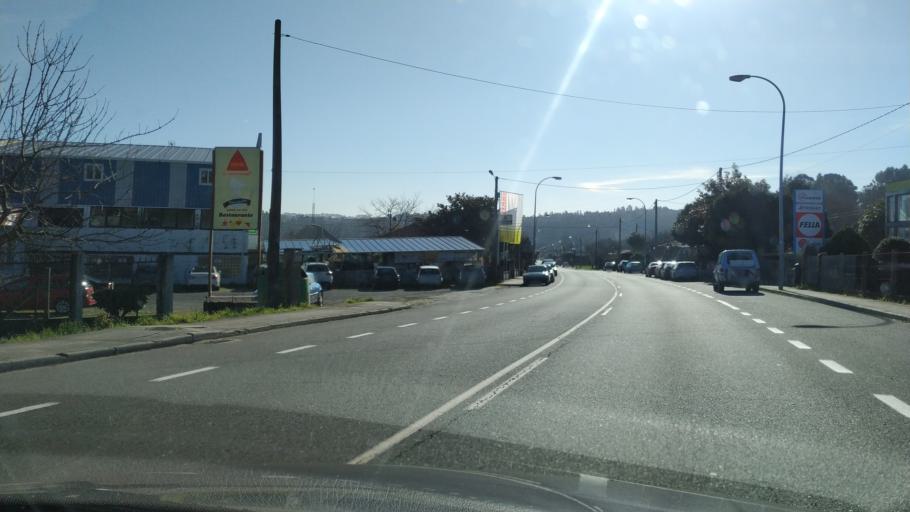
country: ES
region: Galicia
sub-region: Provincia de Pontevedra
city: Silleda
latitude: 42.7396
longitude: -8.3281
